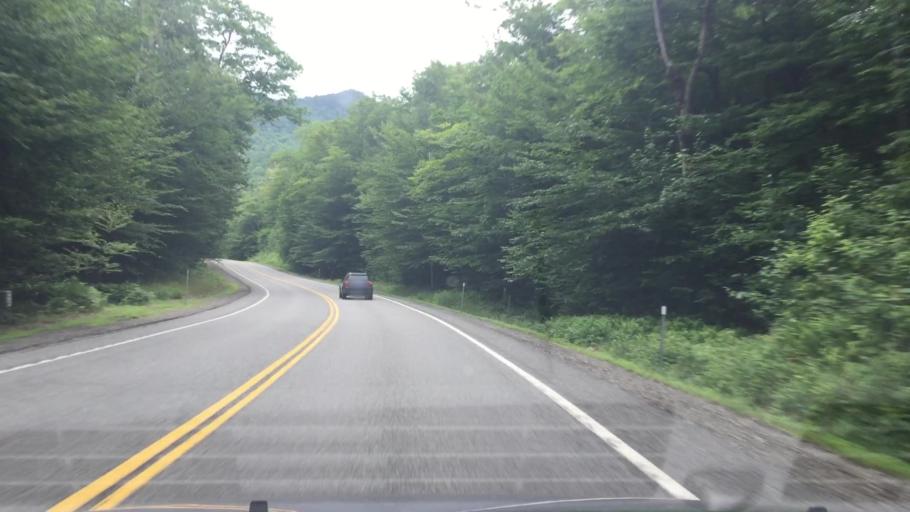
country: US
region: New Hampshire
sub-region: Carroll County
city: North Conway
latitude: 44.0776
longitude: -71.3411
